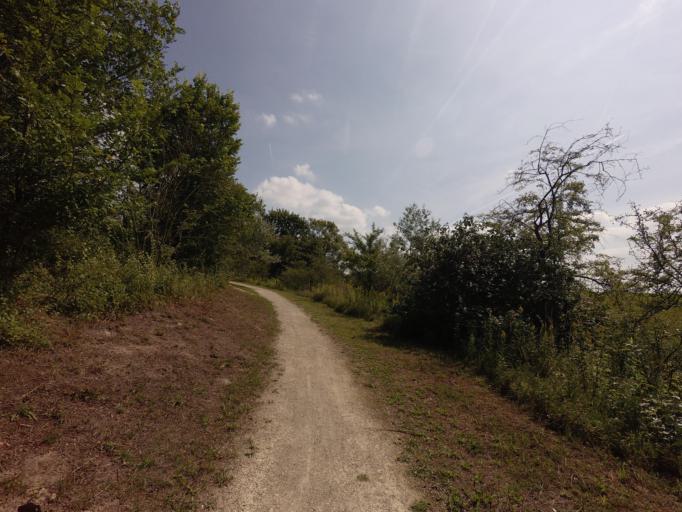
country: NL
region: South Holland
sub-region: Gemeente Sliedrecht
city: Sliedrecht
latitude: 51.7646
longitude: 4.7790
